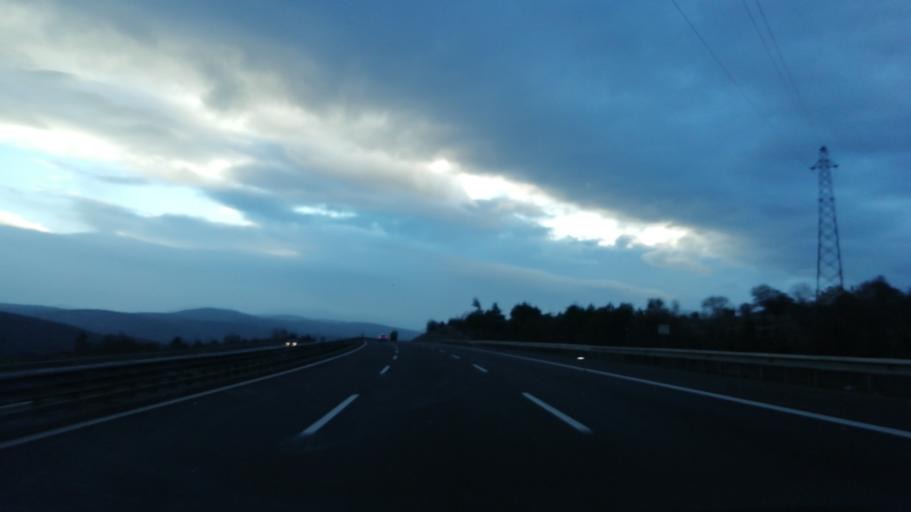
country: TR
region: Bolu
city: Bolu
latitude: 40.7286
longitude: 31.5115
